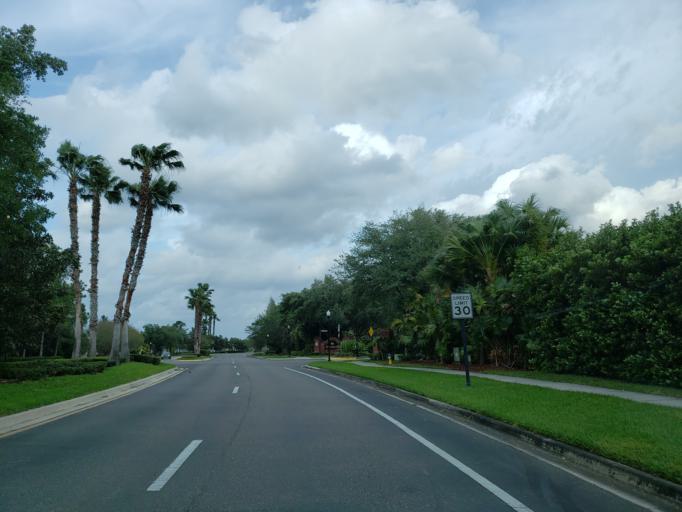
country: US
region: Florida
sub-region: Pasco County
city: Wesley Chapel
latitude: 28.2086
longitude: -82.3577
